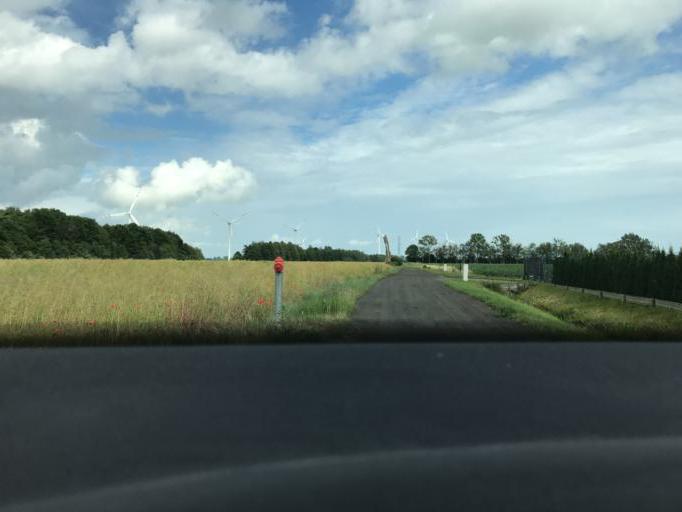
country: PL
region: Pomeranian Voivodeship
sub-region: Gdansk
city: Gdansk
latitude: 54.2982
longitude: 18.7228
